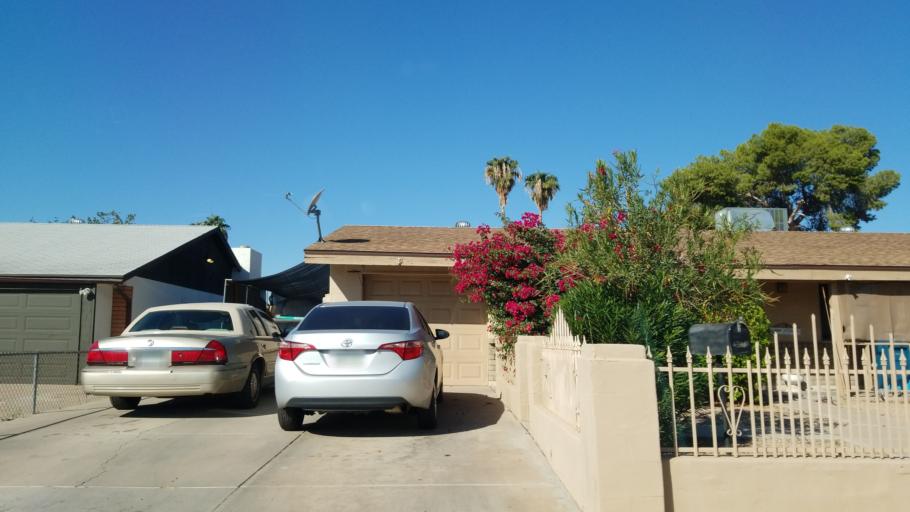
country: US
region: Arizona
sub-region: Maricopa County
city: Glendale
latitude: 33.5003
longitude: -112.2297
